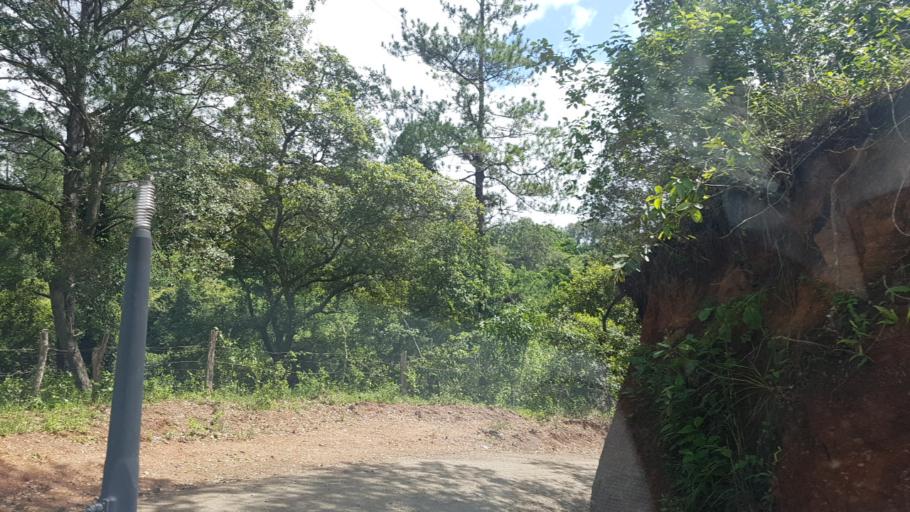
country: NI
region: Nueva Segovia
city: Ciudad Antigua
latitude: 13.6523
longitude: -86.2363
